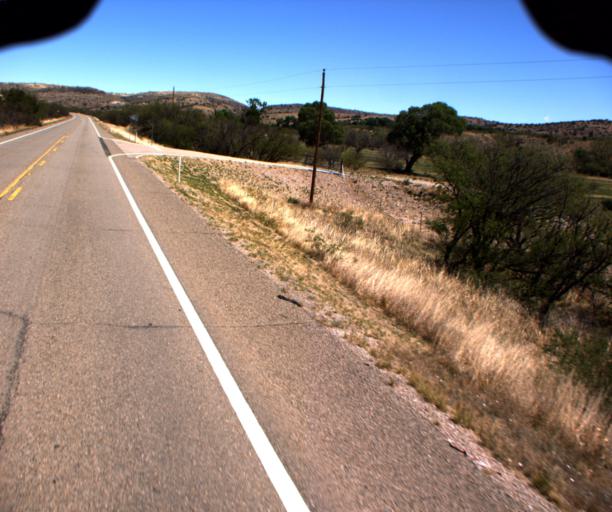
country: US
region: Arizona
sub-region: Santa Cruz County
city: Rio Rico
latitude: 31.6227
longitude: -110.7177
